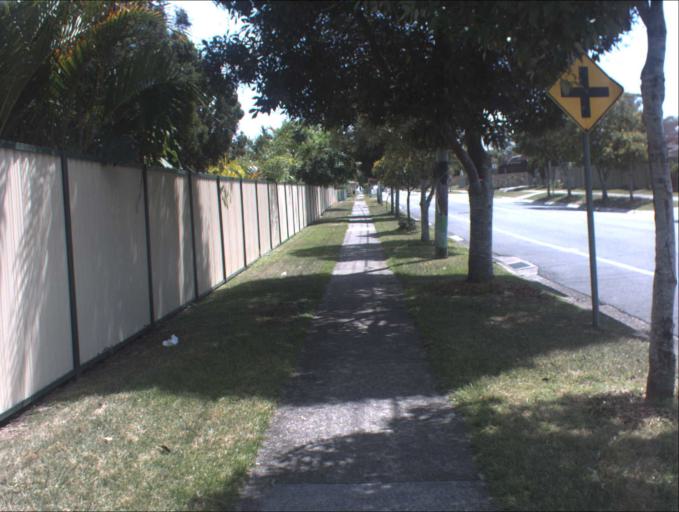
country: AU
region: Queensland
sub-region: Logan
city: Woodridge
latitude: -27.6311
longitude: 153.1031
